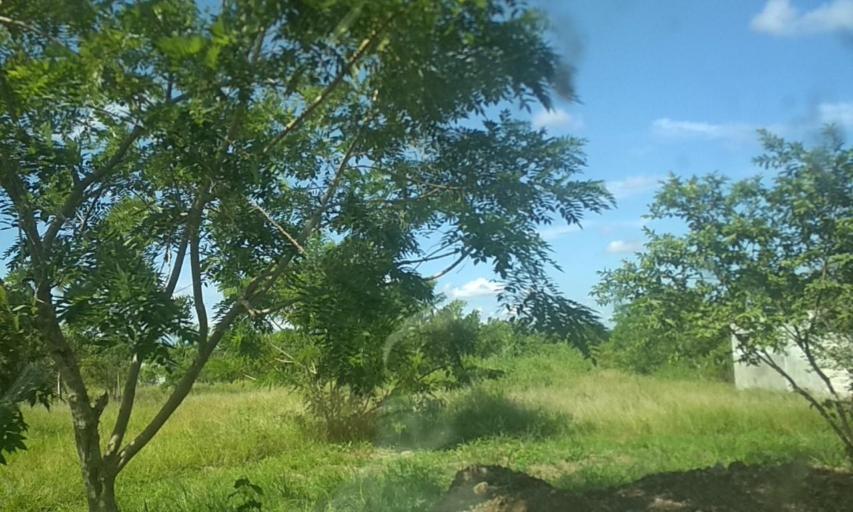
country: MX
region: Veracruz
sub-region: Martinez de la Torre
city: La Union Paso Largo
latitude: 20.1327
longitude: -96.9898
